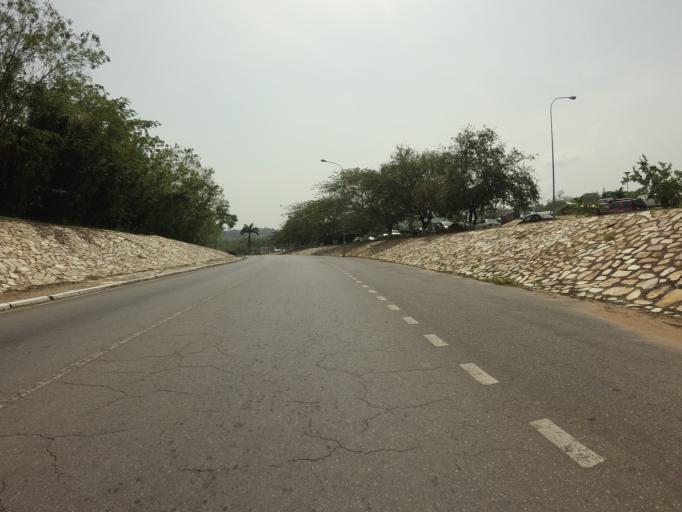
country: GH
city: Akropong
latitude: 6.2649
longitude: 0.0584
